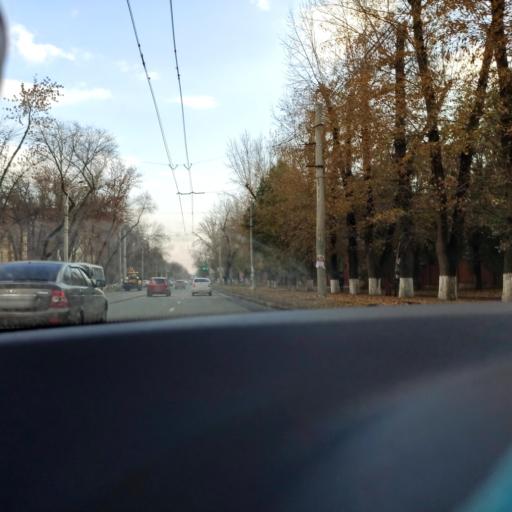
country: RU
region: Samara
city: Samara
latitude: 53.2331
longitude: 50.2452
